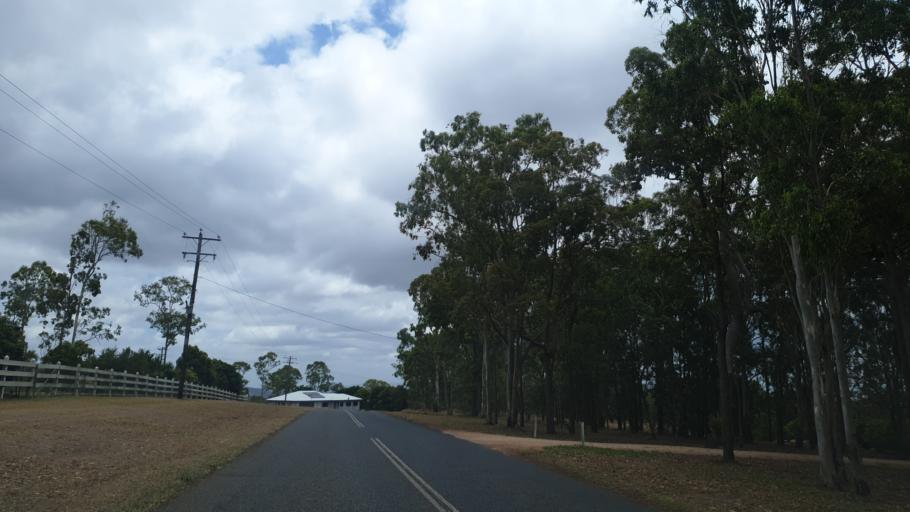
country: AU
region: Queensland
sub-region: Tablelands
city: Tolga
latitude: -17.2109
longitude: 145.4524
